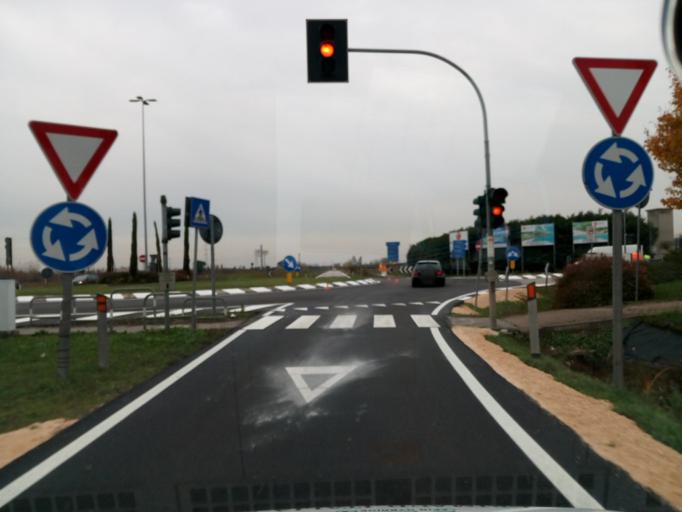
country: IT
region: Veneto
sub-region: Provincia di Padova
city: Saonara
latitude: 45.3734
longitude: 11.9863
